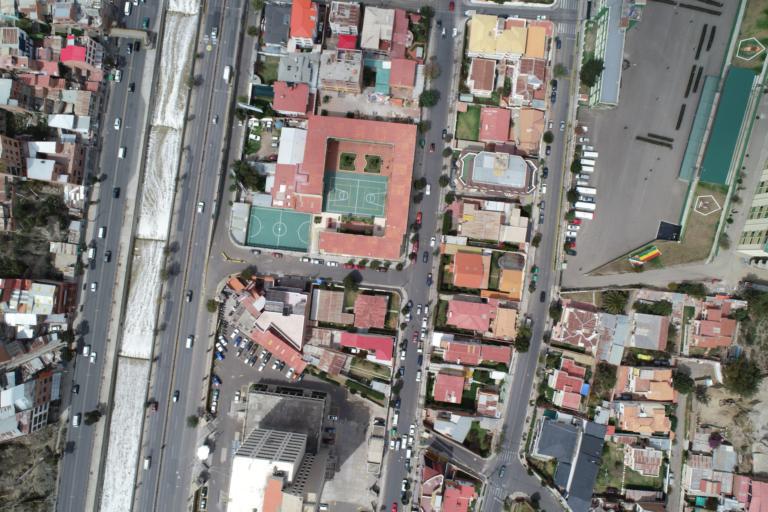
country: BO
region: La Paz
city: La Paz
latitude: -16.5395
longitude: -68.0958
